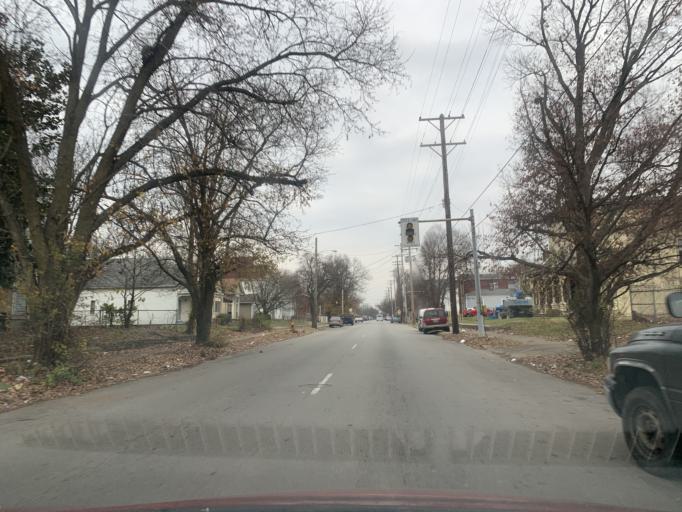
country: US
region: Kentucky
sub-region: Jefferson County
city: Louisville
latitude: 38.2529
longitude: -85.7938
